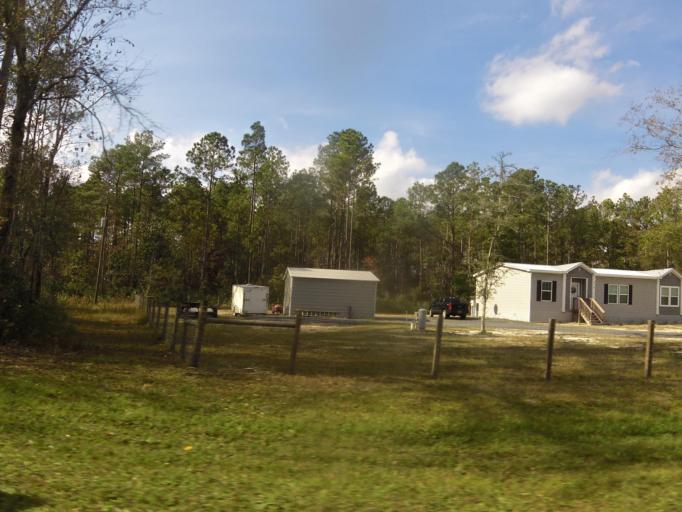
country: US
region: Florida
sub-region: Duval County
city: Baldwin
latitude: 30.1861
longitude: -81.9911
